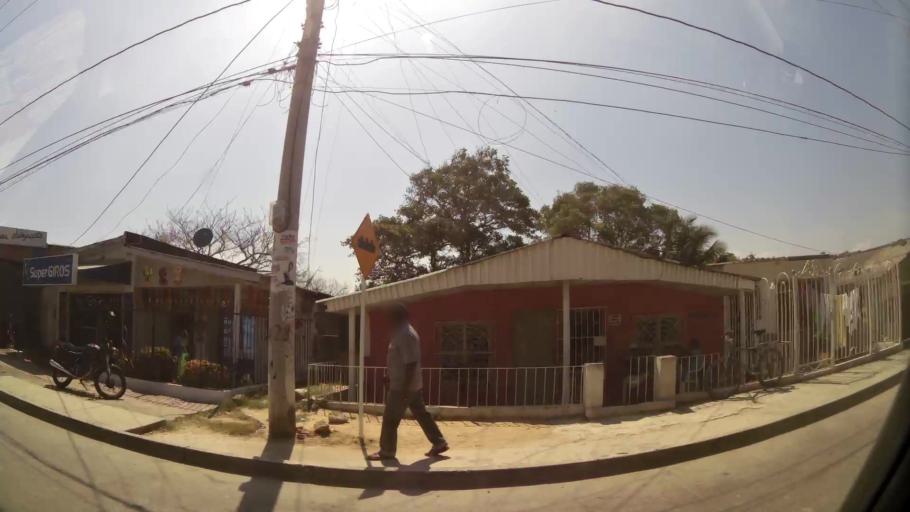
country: CO
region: Atlantico
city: Barranquilla
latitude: 10.9648
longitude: -74.8240
